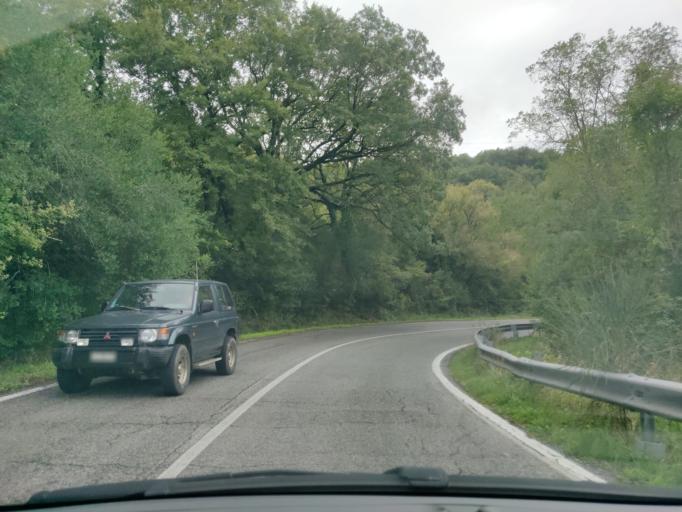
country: IT
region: Latium
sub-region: Citta metropolitana di Roma Capitale
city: Allumiere
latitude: 42.1448
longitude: 11.8885
